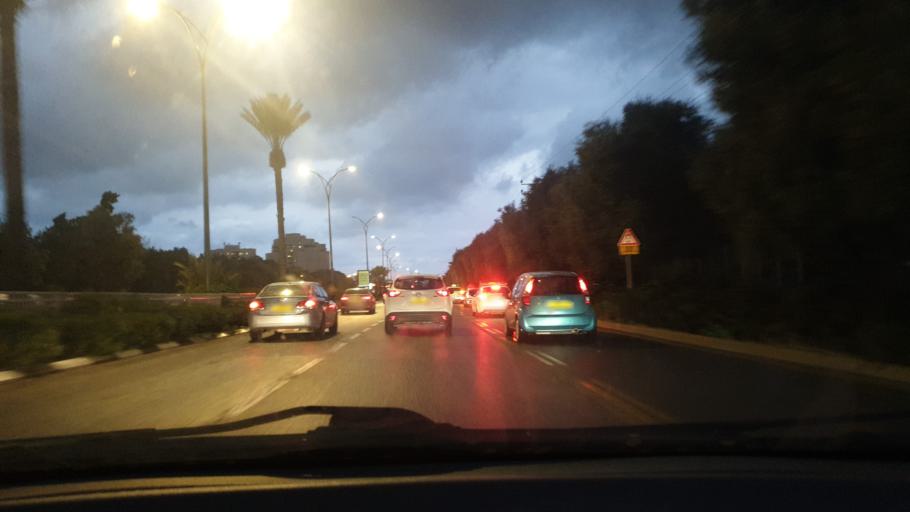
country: IL
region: Central District
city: Rishon LeZiyyon
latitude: 31.9788
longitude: 34.7828
